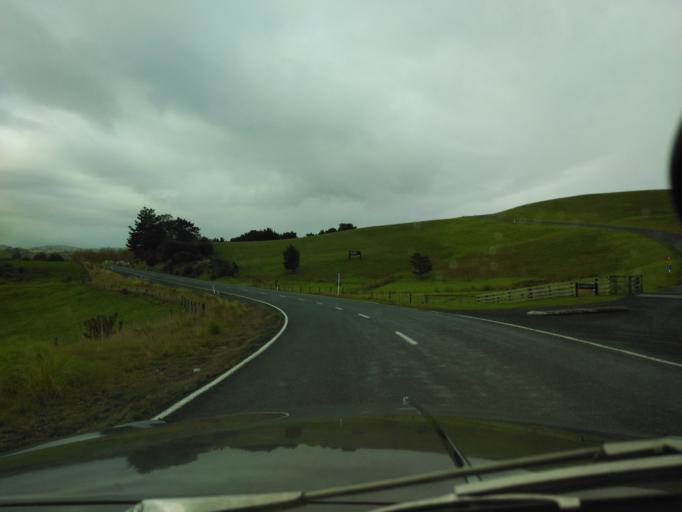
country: NZ
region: Auckland
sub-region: Auckland
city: Wellsford
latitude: -36.3359
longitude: 174.3829
